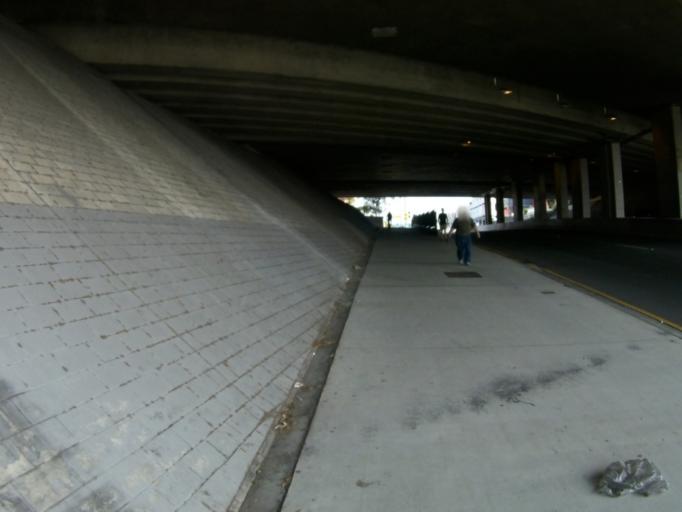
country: AU
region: Queensland
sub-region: Brisbane
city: Woolloongabba
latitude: -27.4977
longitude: 153.0396
